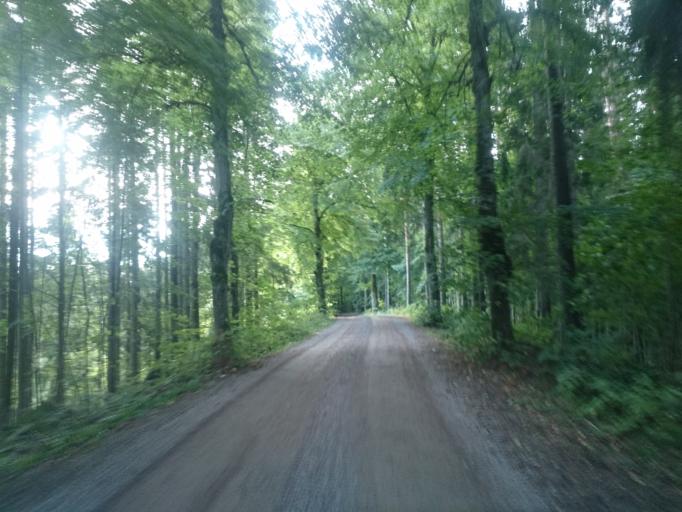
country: SE
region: OEstergoetland
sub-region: Atvidabergs Kommun
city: Atvidaberg
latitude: 58.2712
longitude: 15.9221
